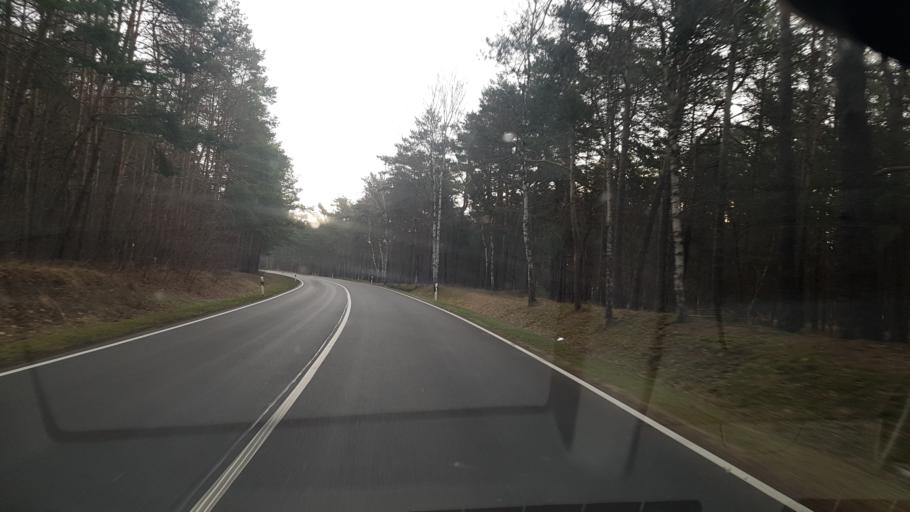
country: DE
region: Brandenburg
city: Vetschau
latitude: 51.7698
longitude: 14.1009
